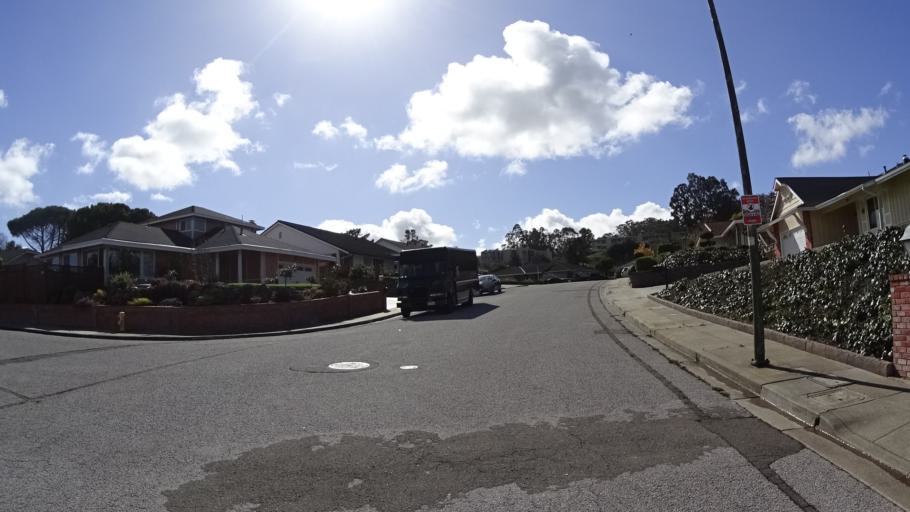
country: US
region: California
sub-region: San Mateo County
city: Millbrae
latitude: 37.5855
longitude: -122.4017
